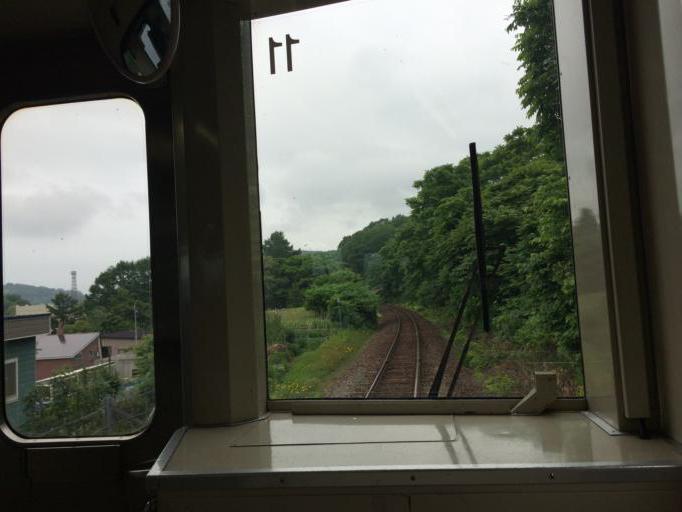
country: JP
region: Hokkaido
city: Otaru
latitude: 43.2118
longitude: 140.9624
